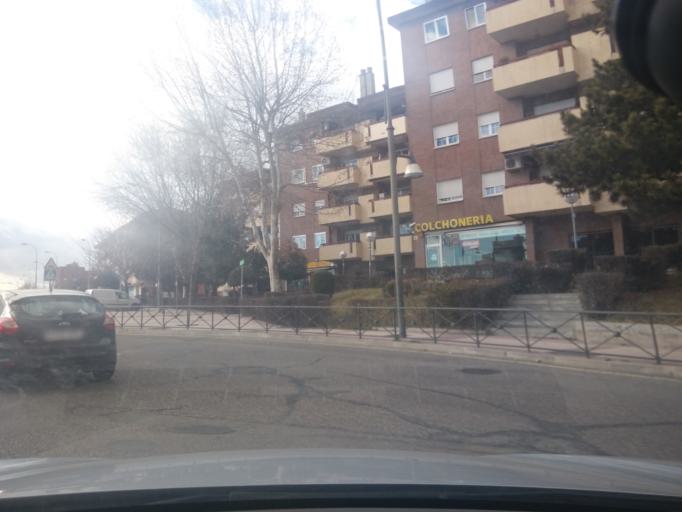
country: ES
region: Madrid
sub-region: Provincia de Madrid
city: Alcobendas
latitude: 40.5465
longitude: -3.6465
